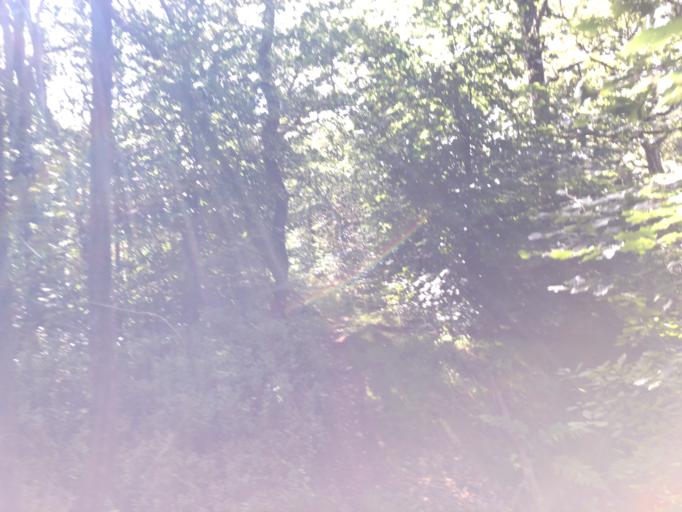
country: DK
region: Central Jutland
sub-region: Holstebro Kommune
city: Ulfborg
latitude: 56.3842
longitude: 8.3604
